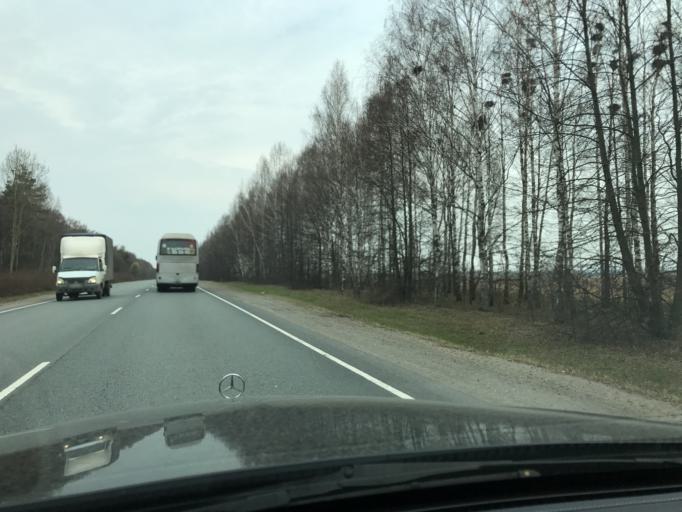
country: RU
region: Vladimir
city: Suzdal'
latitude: 56.3624
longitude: 40.4658
